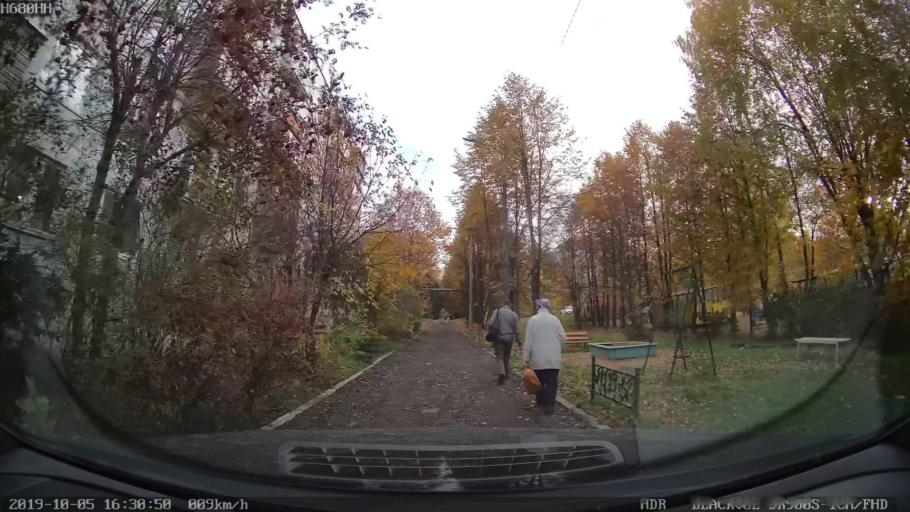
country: RU
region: Moskovskaya
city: Solnechnogorsk
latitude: 56.2185
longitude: 37.0336
